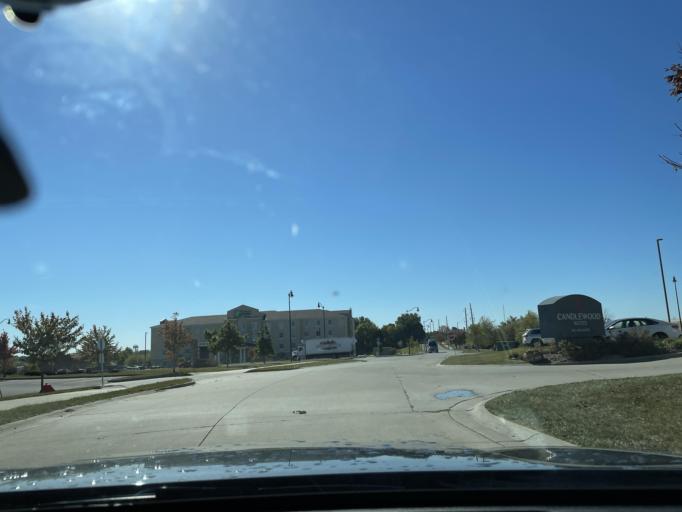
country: US
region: Missouri
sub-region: Andrew County
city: Country Club Village
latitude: 39.8170
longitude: -94.8105
